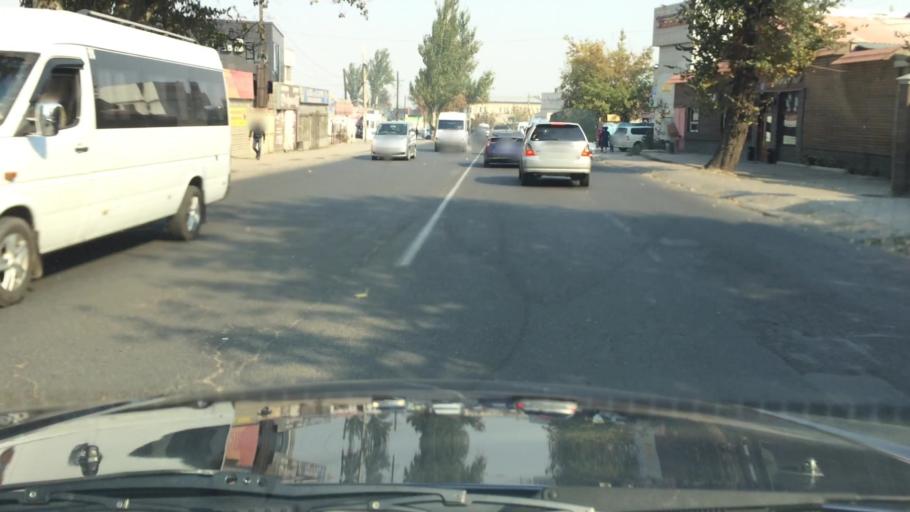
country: KG
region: Chuy
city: Lebedinovka
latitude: 42.8764
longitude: 74.6371
